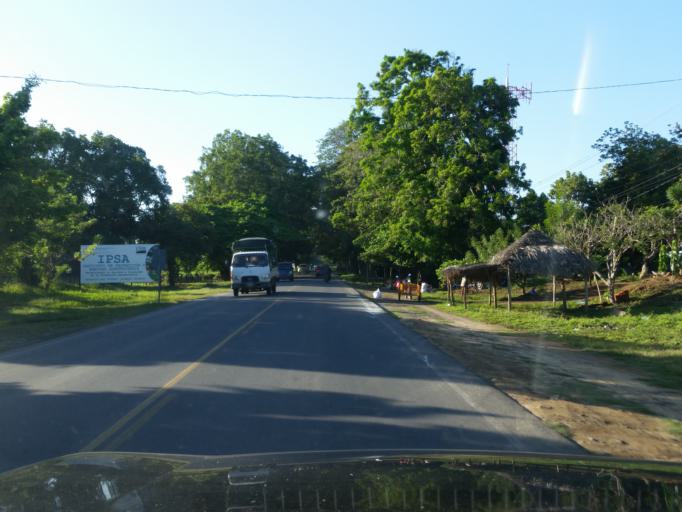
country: NI
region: Rivas
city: Rivas
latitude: 11.4559
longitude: -85.8404
